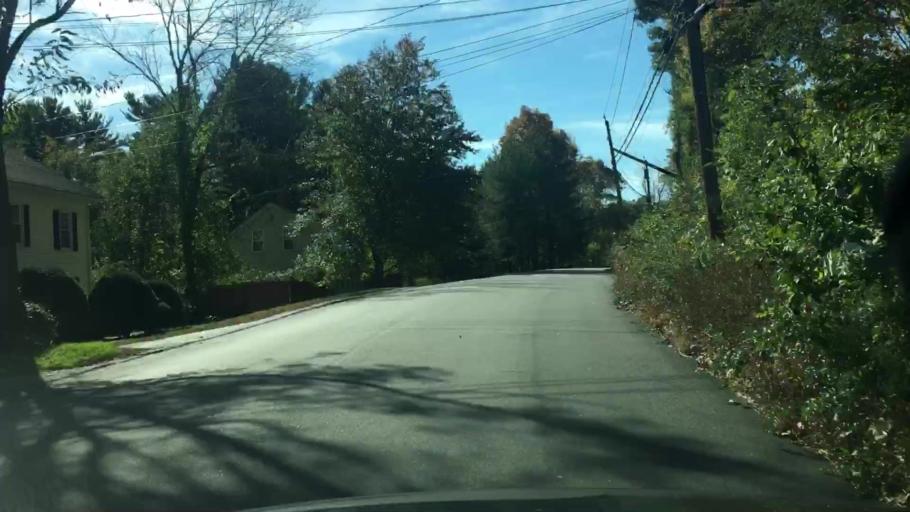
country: US
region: Connecticut
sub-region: Tolland County
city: Stafford Springs
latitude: 41.9654
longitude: -72.2988
